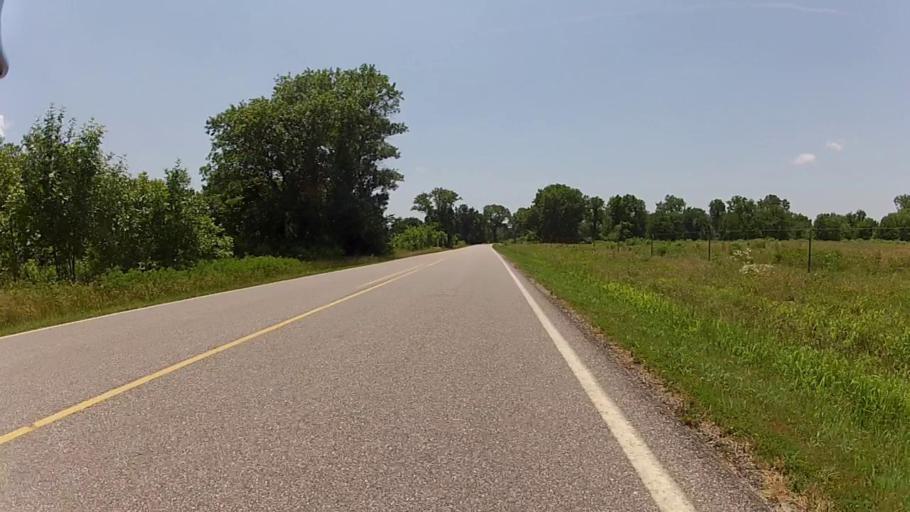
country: US
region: Kansas
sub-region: Montgomery County
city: Cherryvale
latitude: 37.2162
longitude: -95.5384
